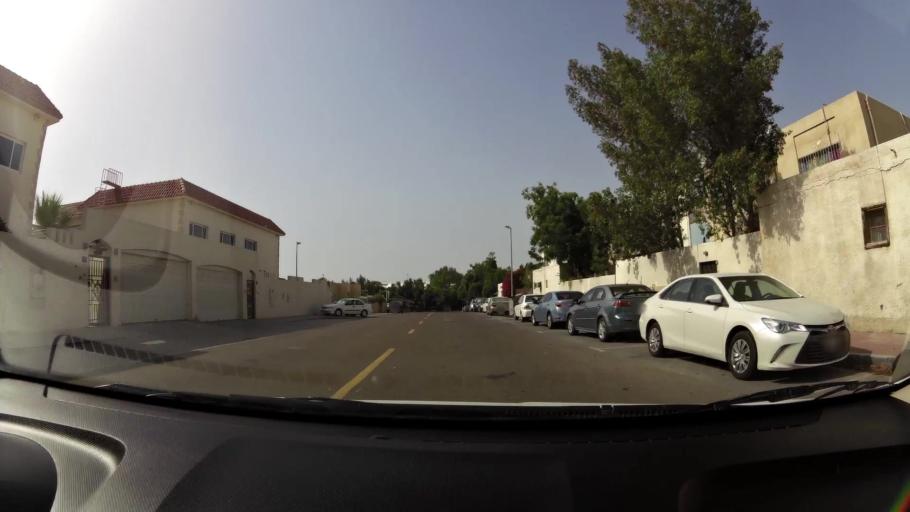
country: AE
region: Ash Shariqah
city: Sharjah
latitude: 25.2429
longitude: 55.3533
